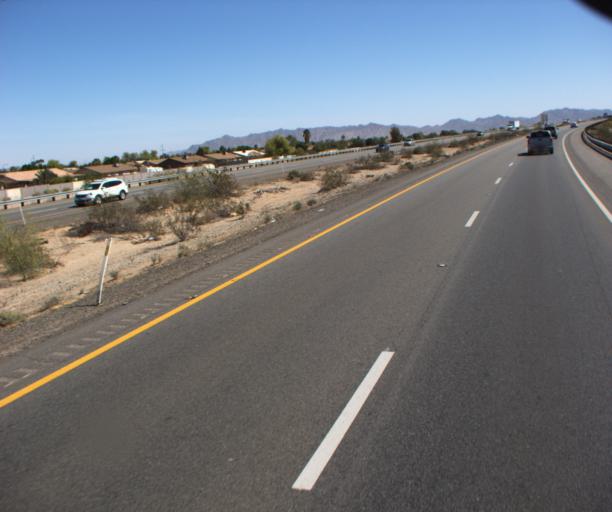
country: US
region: Arizona
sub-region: Yuma County
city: Fortuna Foothills
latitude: 32.6788
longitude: -114.5103
